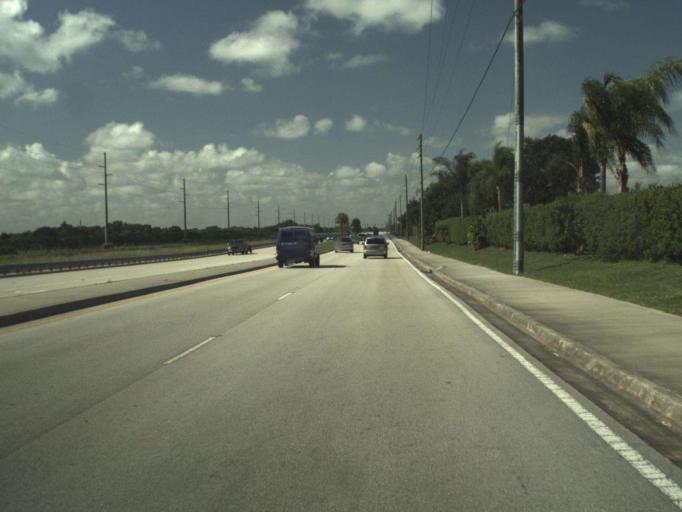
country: US
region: Florida
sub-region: Indian River County
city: Vero Beach South
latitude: 27.6165
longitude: -80.4473
